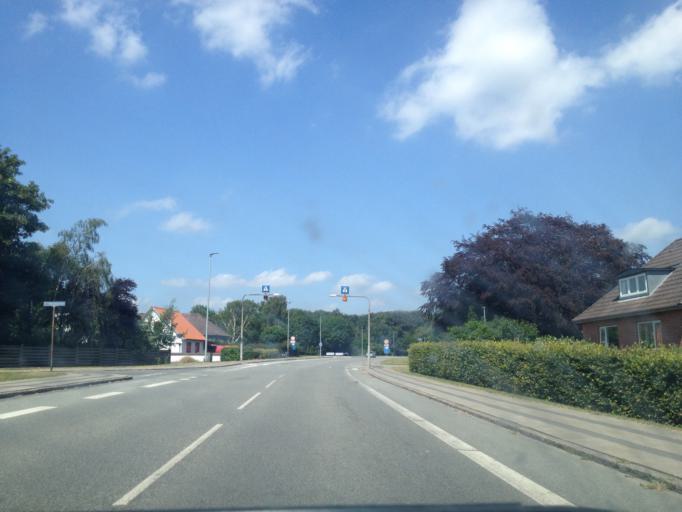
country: DK
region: South Denmark
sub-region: Kolding Kommune
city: Vamdrup
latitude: 55.4317
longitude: 9.2891
